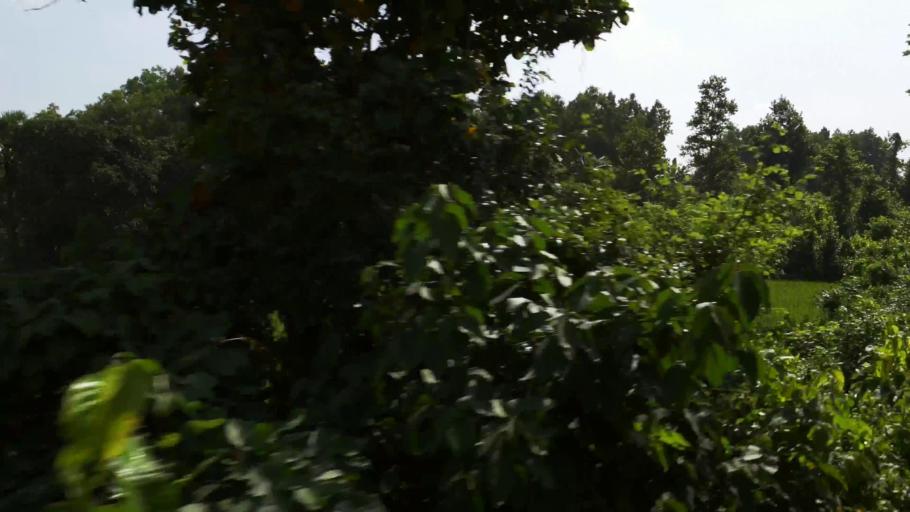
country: BD
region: Dhaka
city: Tungi
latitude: 24.1413
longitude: 90.4623
